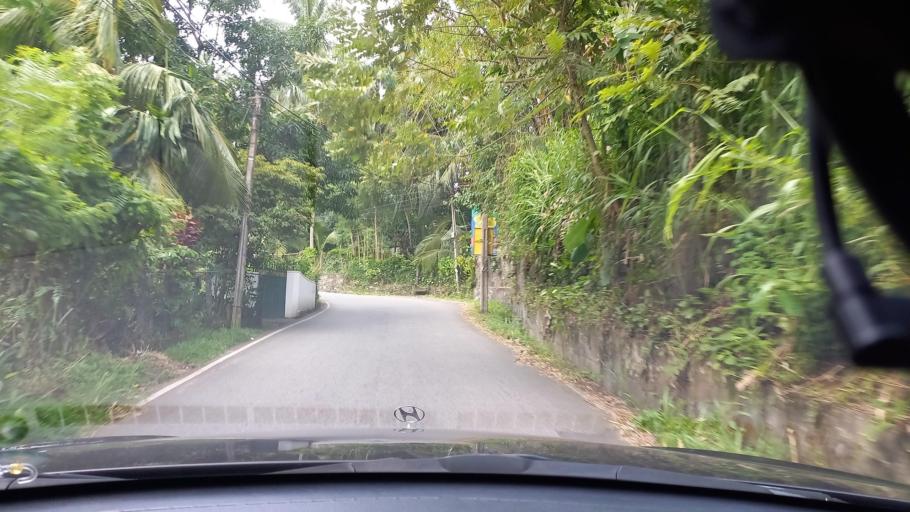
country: LK
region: Central
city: Kadugannawa
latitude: 7.2569
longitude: 80.3545
